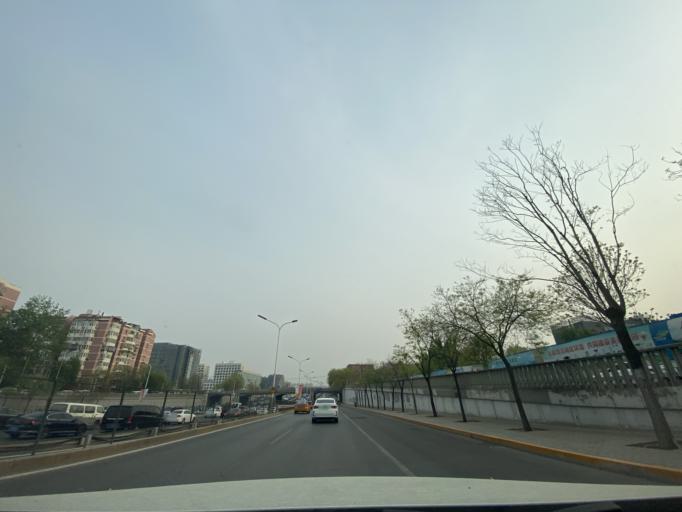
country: CN
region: Beijing
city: Sijiqing
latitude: 39.9348
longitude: 116.2681
